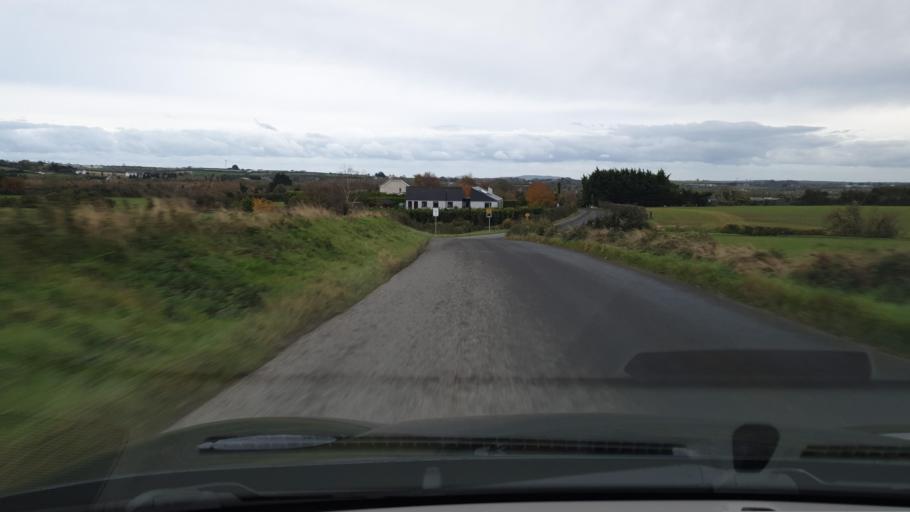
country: IE
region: Leinster
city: Balrothery
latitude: 53.5503
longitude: -6.2291
